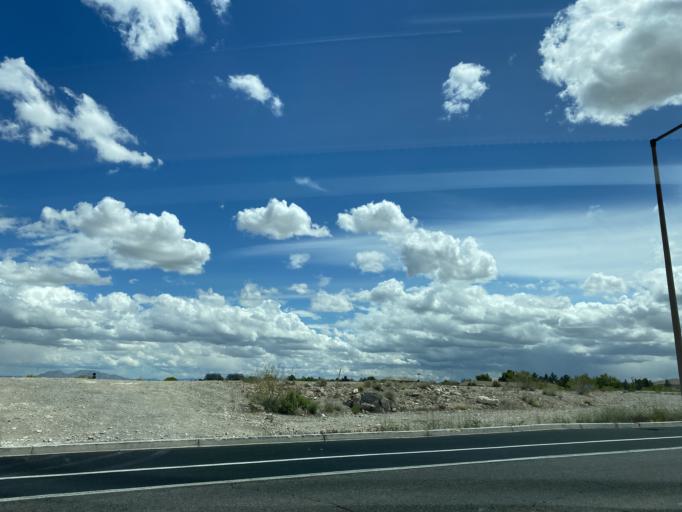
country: US
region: Nevada
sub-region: Clark County
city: Summerlin South
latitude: 36.1708
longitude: -115.3156
